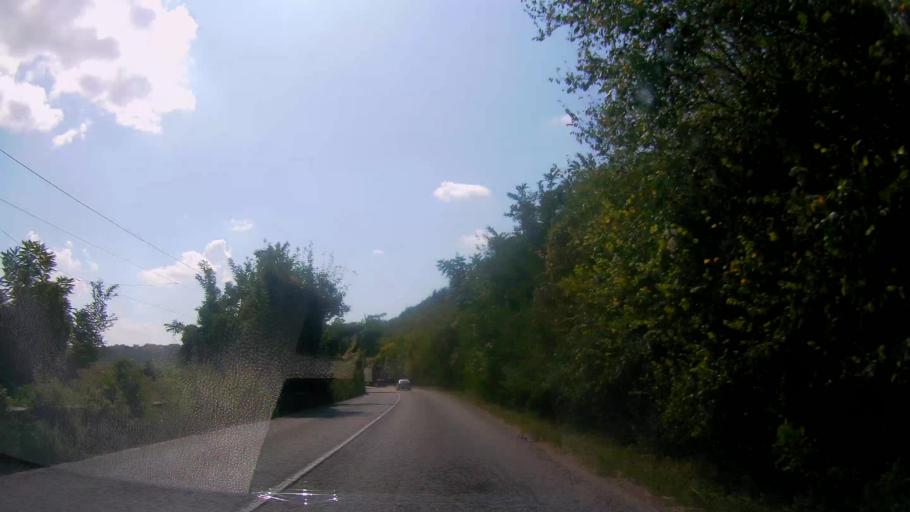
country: BG
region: Veliko Turnovo
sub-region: Obshtina Polski Trumbesh
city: Polski Trumbesh
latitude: 43.4375
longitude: 25.6543
